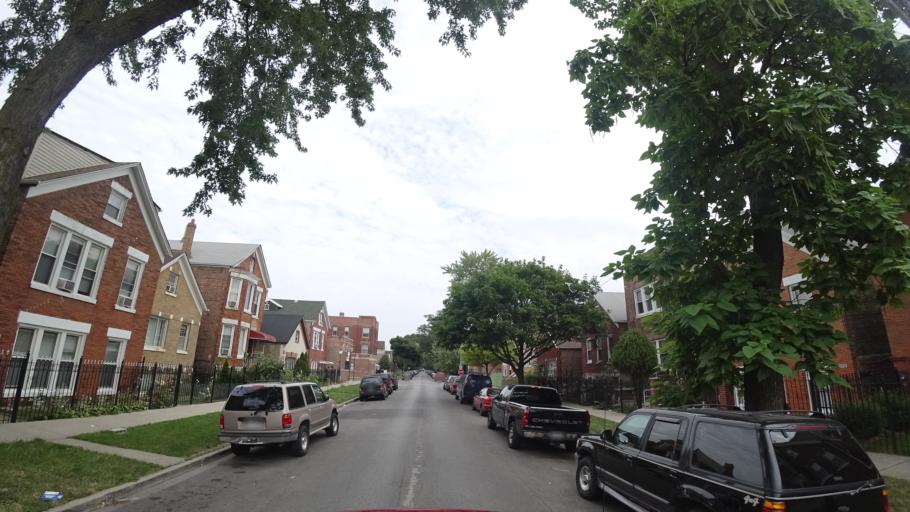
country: US
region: Illinois
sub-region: Cook County
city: Cicero
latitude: 41.8383
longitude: -87.7122
